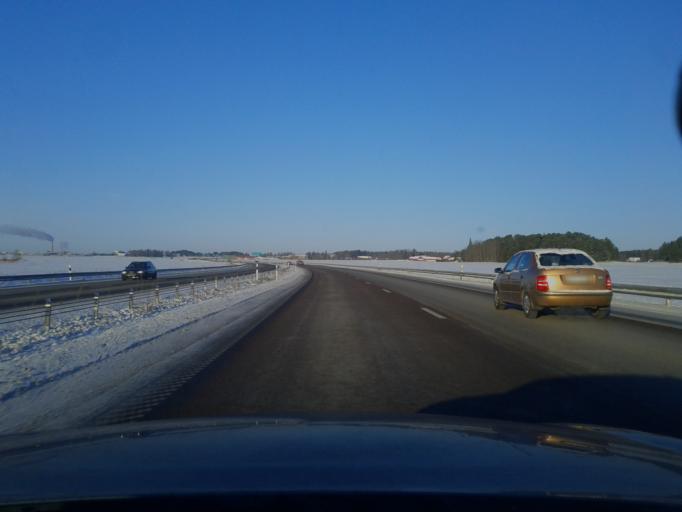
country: SE
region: Uppsala
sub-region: Uppsala Kommun
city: Saevja
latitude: 59.8203
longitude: 17.7516
